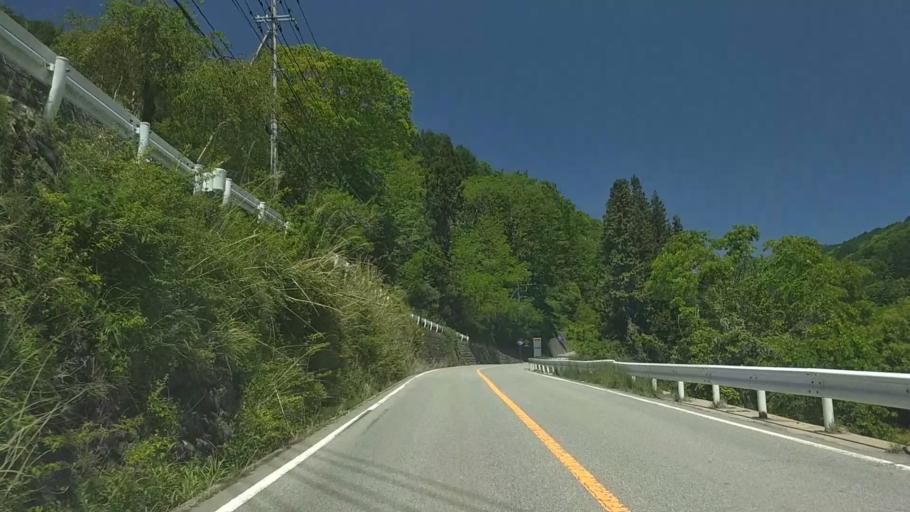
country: JP
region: Yamanashi
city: Nirasaki
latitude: 35.8748
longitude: 138.4288
